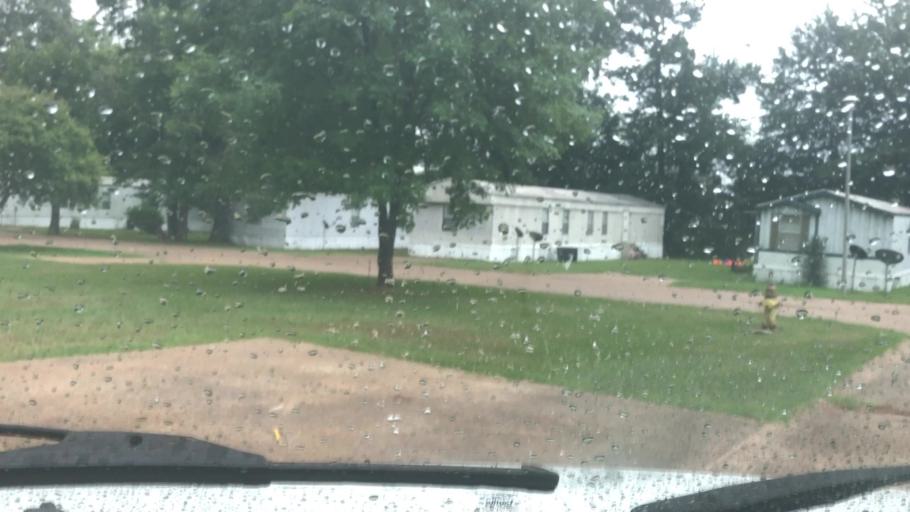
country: US
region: Texas
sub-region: Bowie County
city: Wake Village
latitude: 33.3872
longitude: -94.0785
